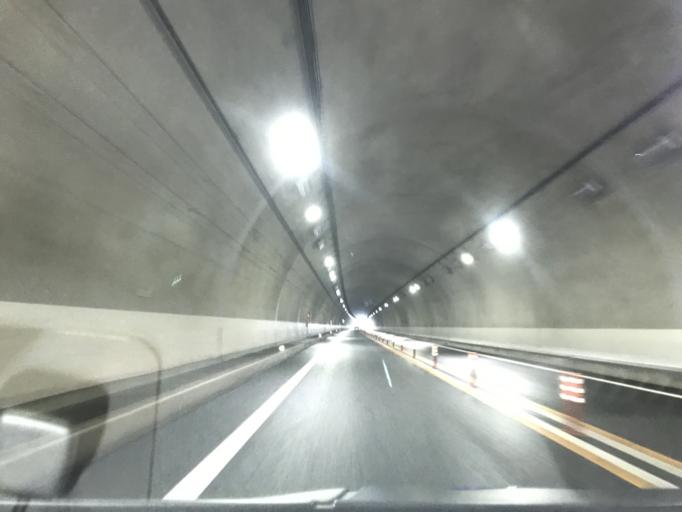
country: JP
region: Fukuoka
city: Nakatsu
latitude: 33.5141
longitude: 131.2793
